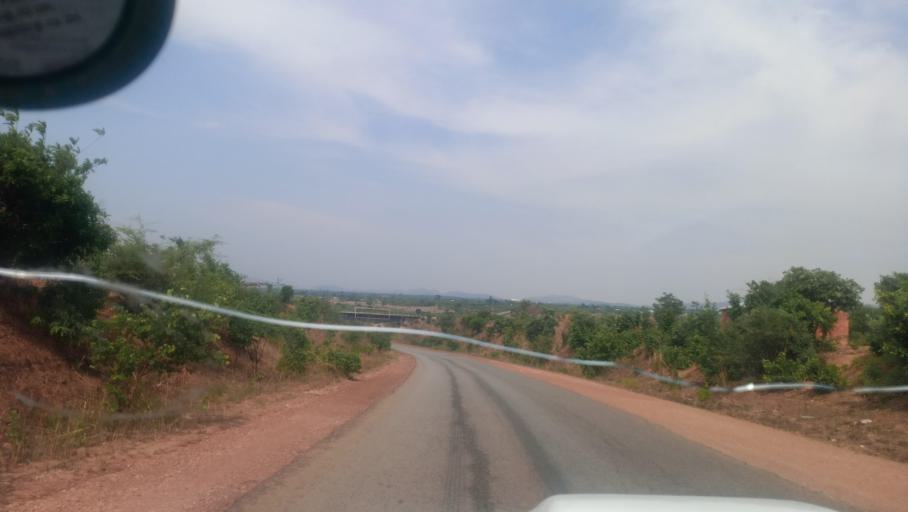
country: ZM
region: Northern
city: Mpika
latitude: -11.8360
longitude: 31.3881
